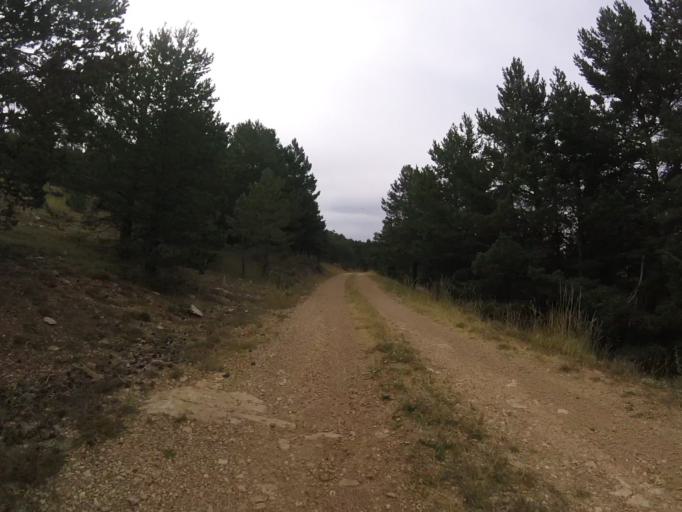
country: ES
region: Aragon
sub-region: Provincia de Teruel
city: Valdelinares
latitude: 40.3566
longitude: -0.5991
